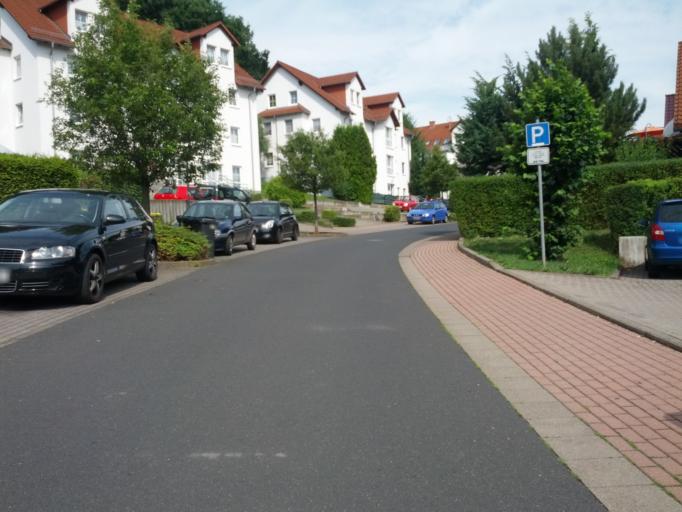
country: DE
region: Thuringia
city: Krauthausen
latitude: 51.0193
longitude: 10.2688
